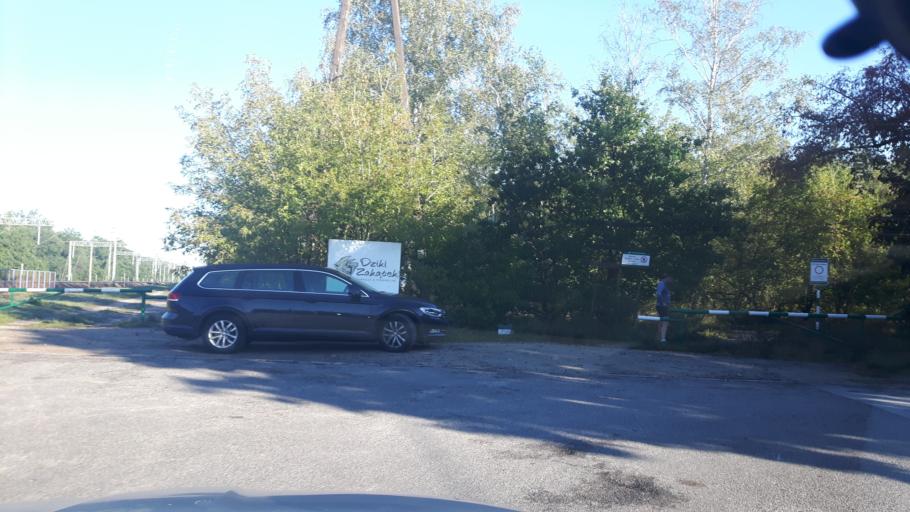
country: PL
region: Masovian Voivodeship
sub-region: Warszawa
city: Bialoleka
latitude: 52.3588
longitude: 20.9721
